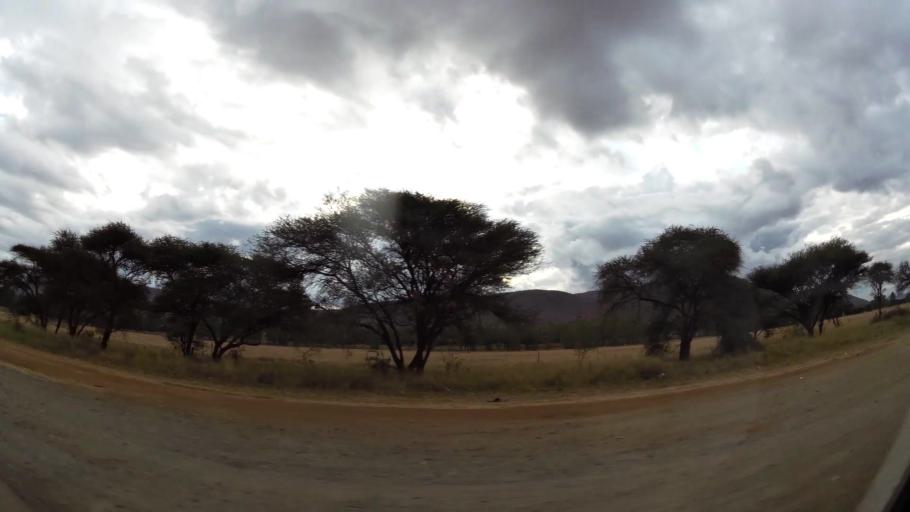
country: ZA
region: Limpopo
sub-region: Waterberg District Municipality
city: Mokopane
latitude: -24.2708
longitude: 28.9812
